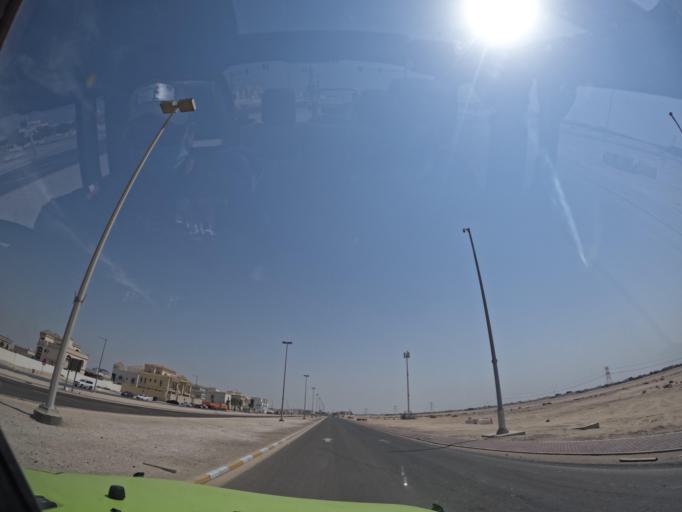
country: AE
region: Abu Dhabi
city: Abu Dhabi
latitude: 24.3048
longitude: 54.5433
